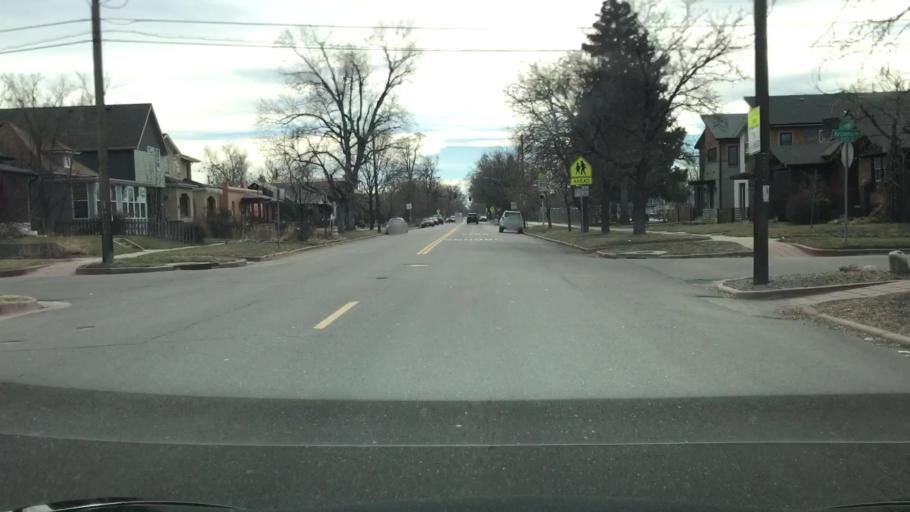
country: US
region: Colorado
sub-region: Denver County
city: Denver
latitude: 39.6950
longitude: -104.9828
